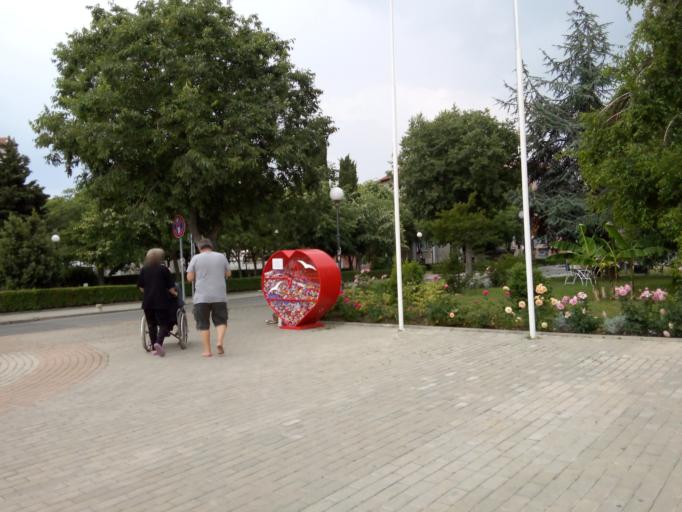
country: BG
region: Burgas
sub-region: Obshtina Pomorie
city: Pomorie
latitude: 42.5587
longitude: 27.6417
